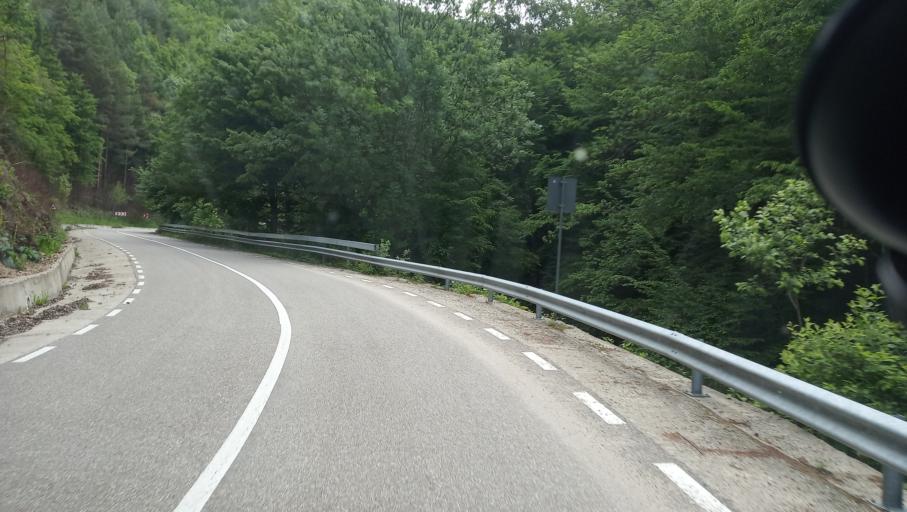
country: RO
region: Caras-Severin
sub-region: Comuna Slatina-Timis
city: Slatina-Timis
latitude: 45.2616
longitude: 22.2360
